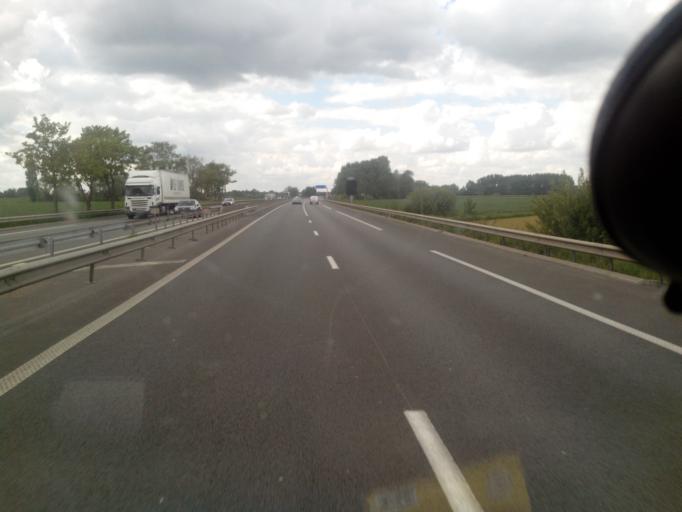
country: FR
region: Nord-Pas-de-Calais
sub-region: Departement du Nord
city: Nieppe
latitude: 50.6915
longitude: 2.8160
